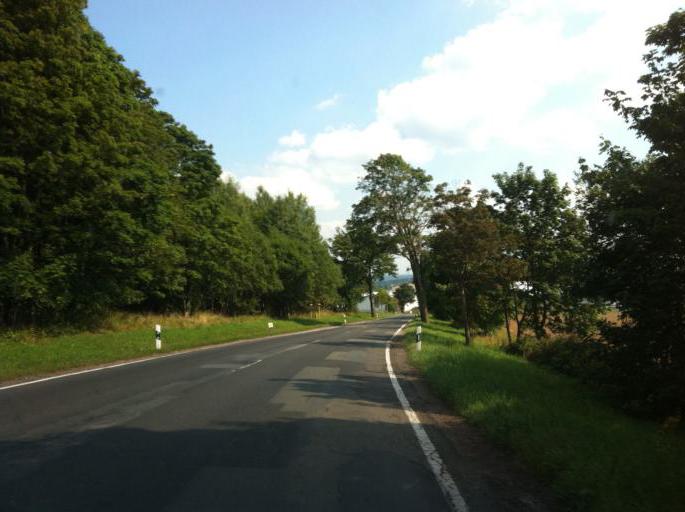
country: DE
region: Thuringia
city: Grossbreitenbach
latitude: 50.5918
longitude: 10.9877
